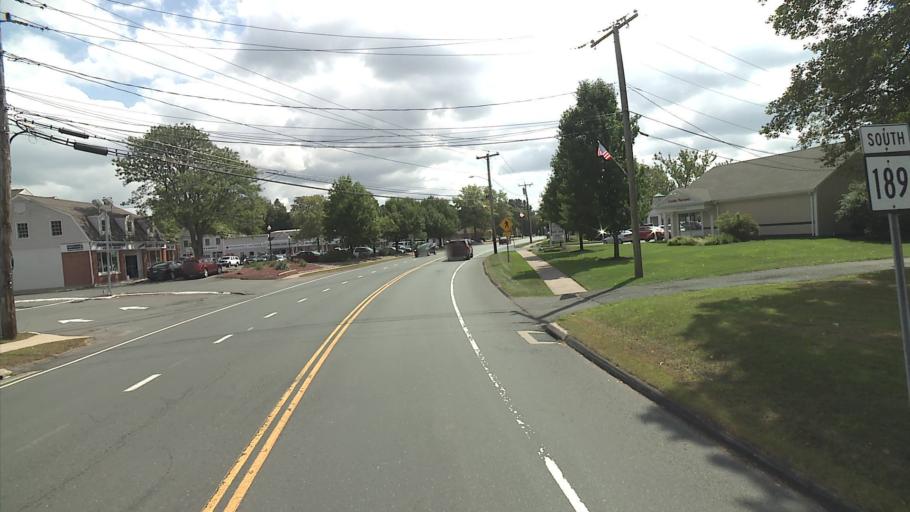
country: US
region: Connecticut
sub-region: Hartford County
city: Salmon Brook
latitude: 41.9526
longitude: -72.7885
